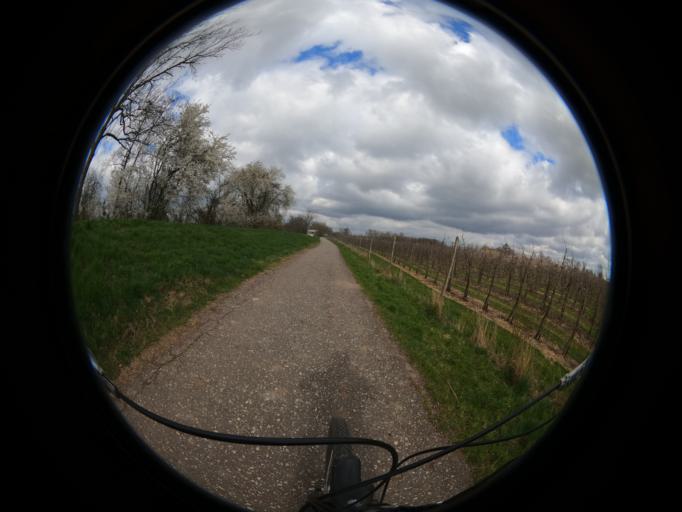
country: DE
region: Lower Saxony
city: Neu Wulmstorf
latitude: 53.5239
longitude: 9.8240
